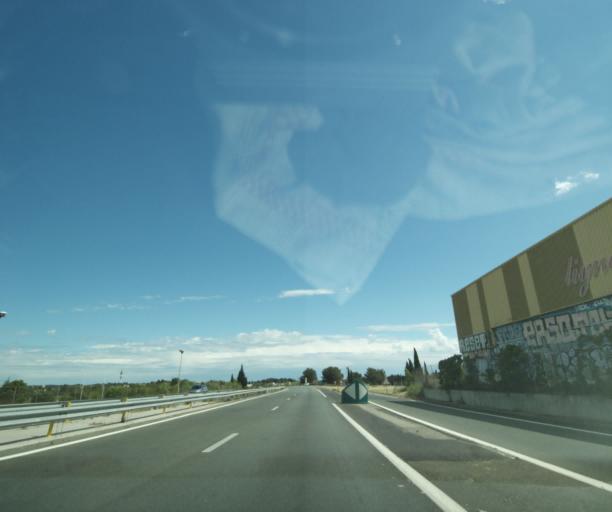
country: FR
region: Languedoc-Roussillon
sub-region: Departement de l'Herault
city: Juvignac
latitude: 43.6203
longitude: 3.7912
